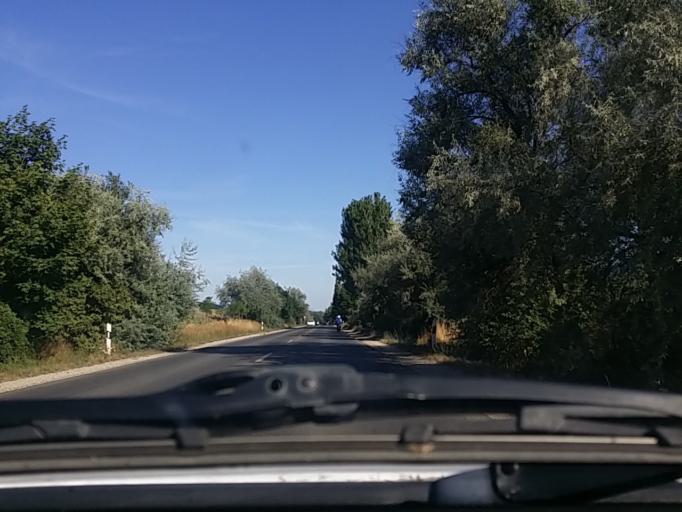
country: HU
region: Pest
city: Solymar
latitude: 47.6037
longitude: 18.9523
